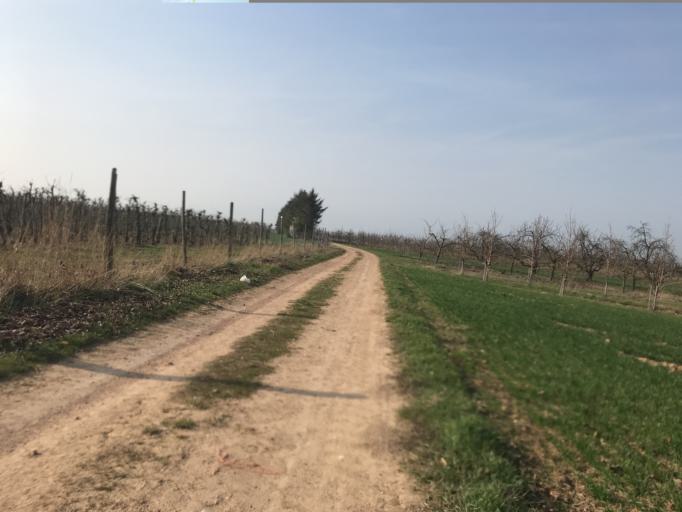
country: DE
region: Rheinland-Pfalz
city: Wackernheim
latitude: 49.9841
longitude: 8.1366
